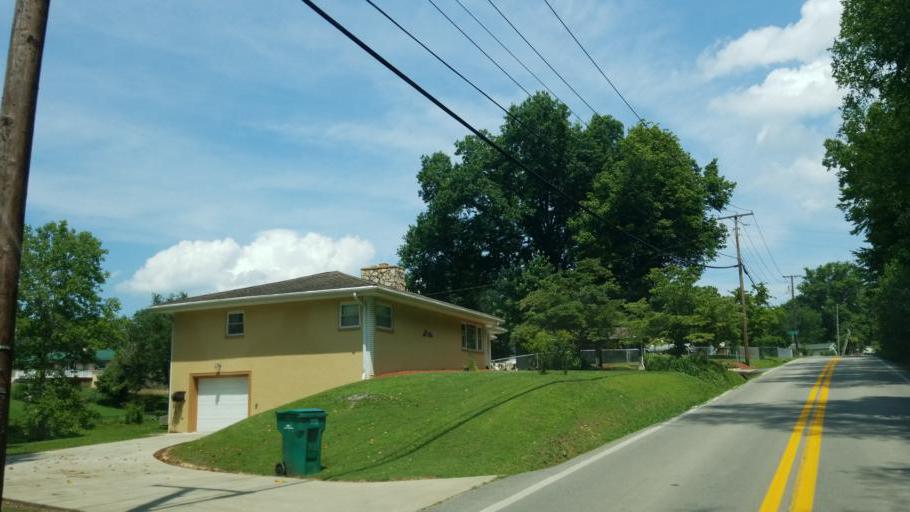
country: US
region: West Virginia
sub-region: Kanawha County
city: Nitro
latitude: 38.4537
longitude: -81.8763
